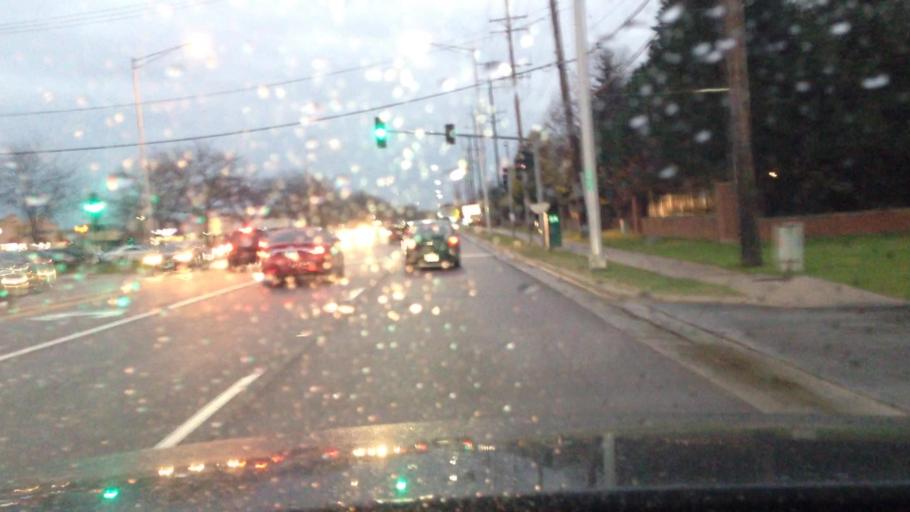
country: US
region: Illinois
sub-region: Cook County
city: Rolling Meadows
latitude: 42.0578
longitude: -88.0079
